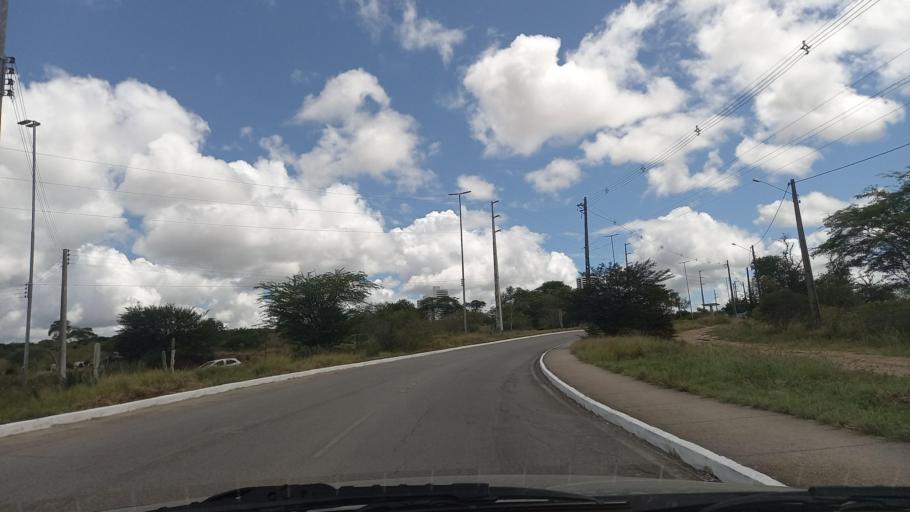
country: BR
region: Pernambuco
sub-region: Caruaru
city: Caruaru
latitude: -8.2932
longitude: -35.9424
